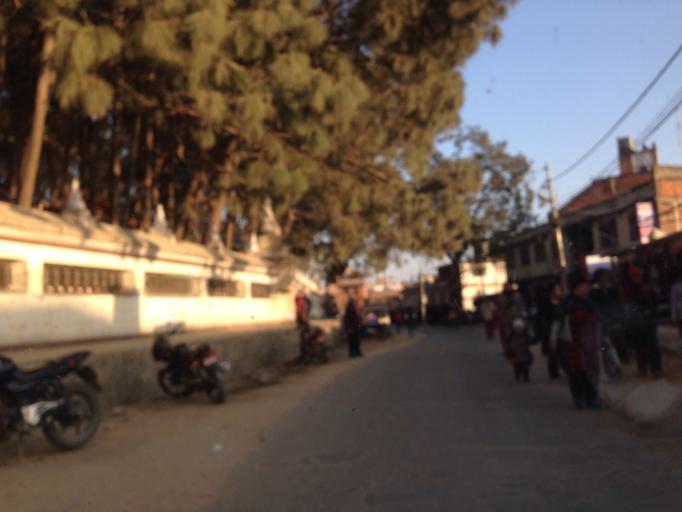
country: NP
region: Central Region
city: Kirtipur
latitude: 27.7158
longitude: 85.2843
